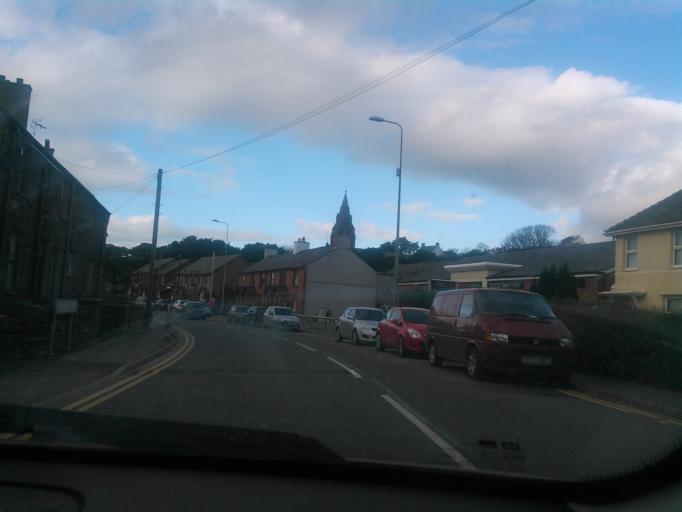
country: GB
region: Wales
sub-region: Gwynedd
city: Bethesda
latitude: 53.1781
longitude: -4.0581
